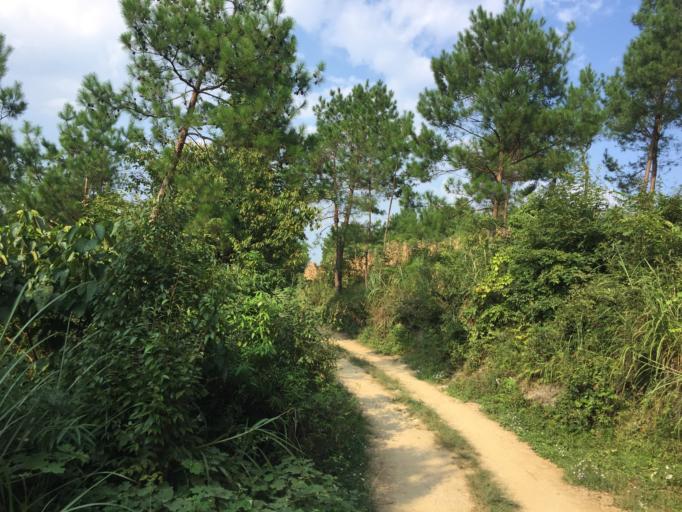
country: CN
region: Guizhou Sheng
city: Shiqian
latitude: 27.6060
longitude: 108.0157
